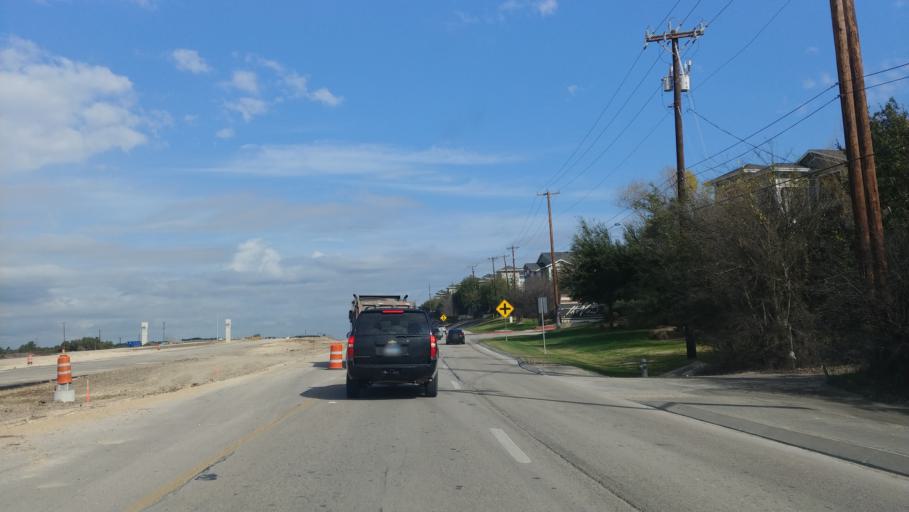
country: US
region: Texas
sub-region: Bexar County
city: Leon Valley
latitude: 29.4606
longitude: -98.7111
